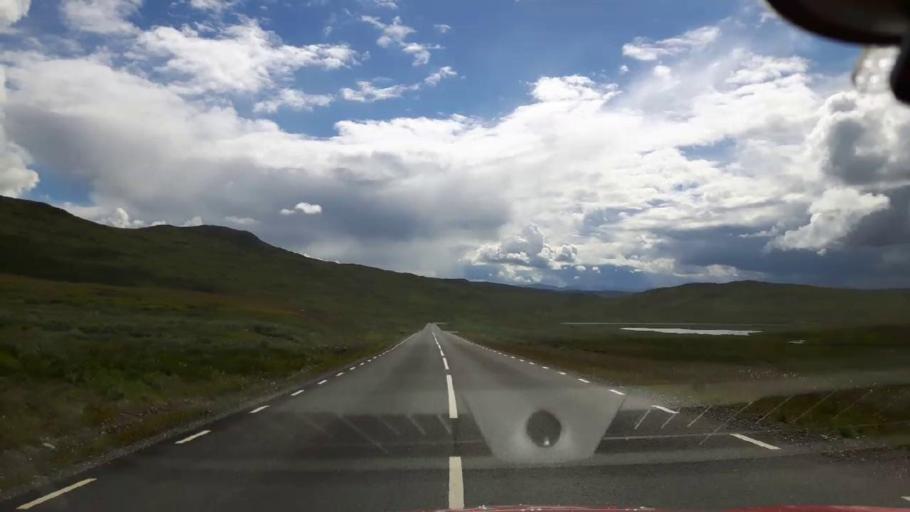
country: NO
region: Nordland
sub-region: Hattfjelldal
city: Hattfjelldal
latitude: 65.0361
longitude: 14.3288
